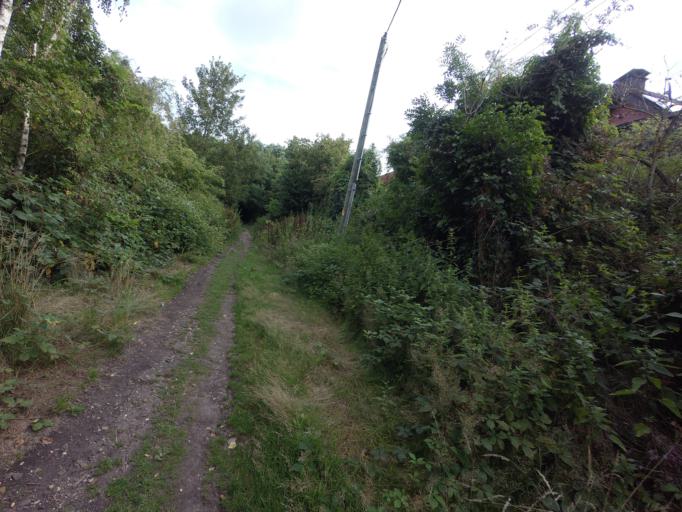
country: DE
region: North Rhine-Westphalia
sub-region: Regierungsbezirk Koln
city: Alsdorf
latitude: 50.8673
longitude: 6.1342
